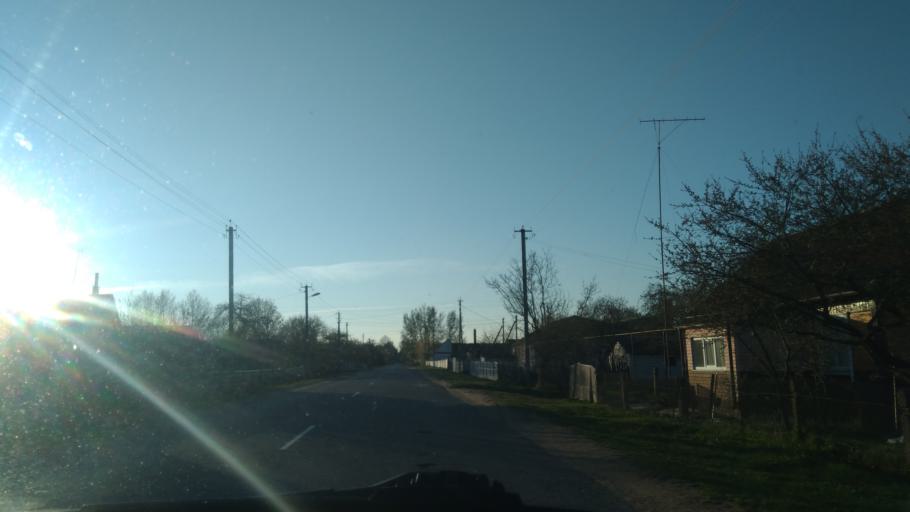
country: BY
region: Minsk
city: Haradzyeya
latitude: 53.3599
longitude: 26.5358
